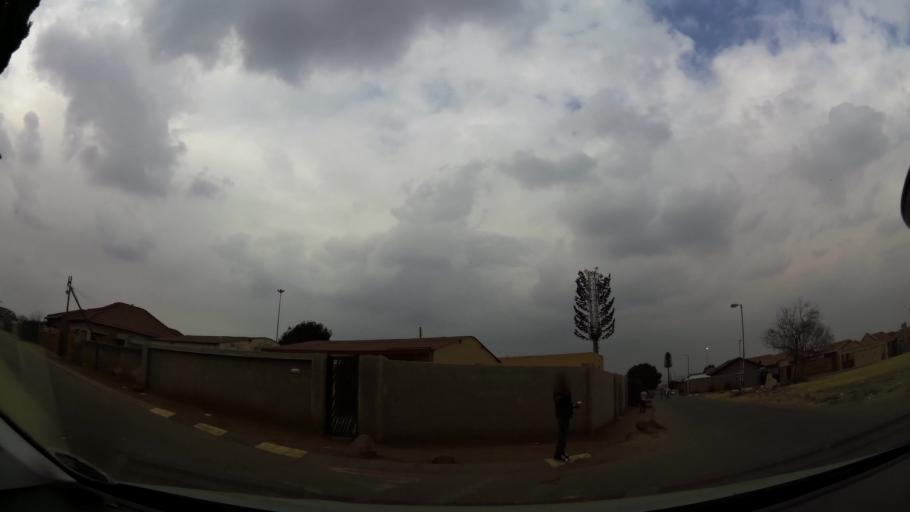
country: ZA
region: Gauteng
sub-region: City of Johannesburg Metropolitan Municipality
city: Soweto
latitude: -26.2571
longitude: 27.8605
